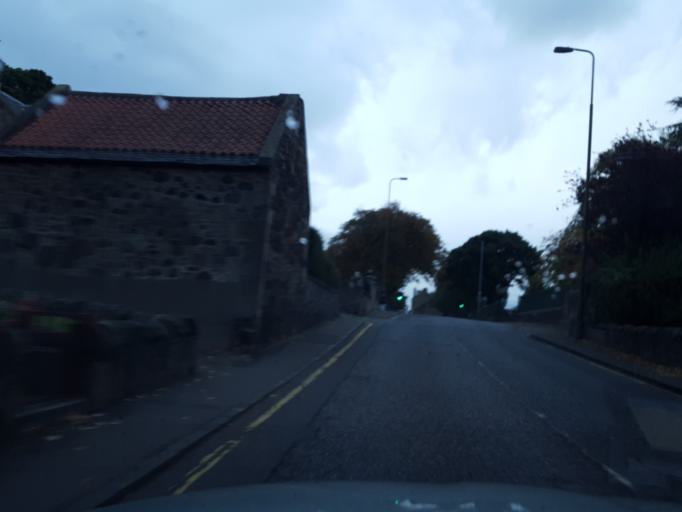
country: GB
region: Scotland
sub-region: Edinburgh
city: Colinton
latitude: 55.9401
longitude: -3.2870
